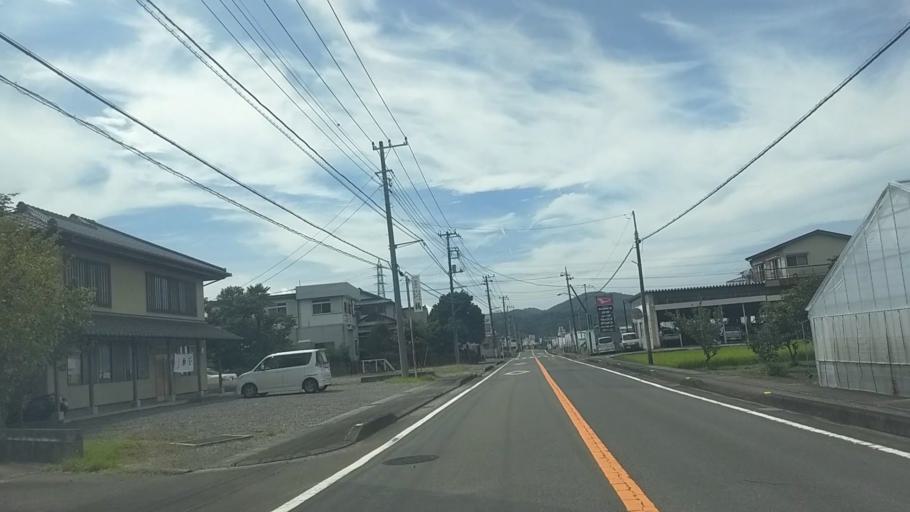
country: JP
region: Shizuoka
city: Mishima
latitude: 35.0374
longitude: 138.9572
